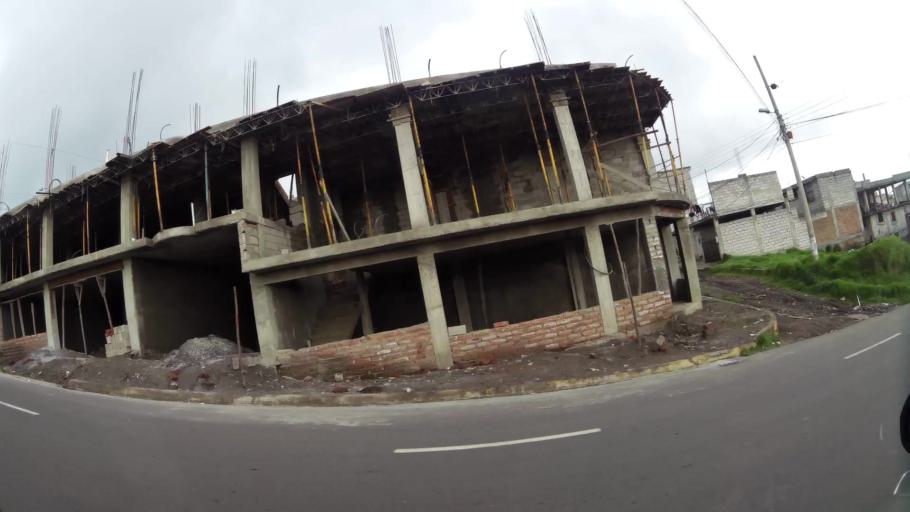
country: EC
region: Pichincha
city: Sangolqui
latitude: -0.3088
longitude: -78.5253
